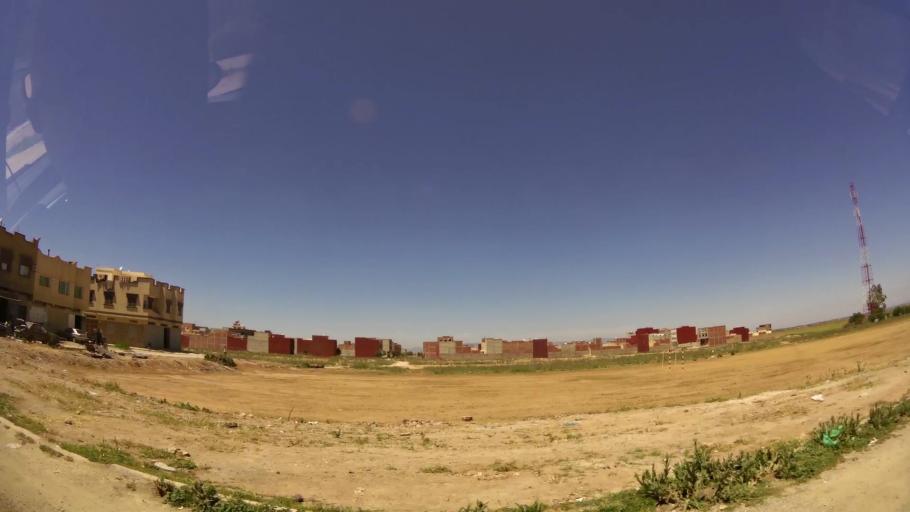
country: MA
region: Oriental
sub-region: Oujda-Angad
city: Oujda
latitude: 34.6779
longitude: -1.8557
